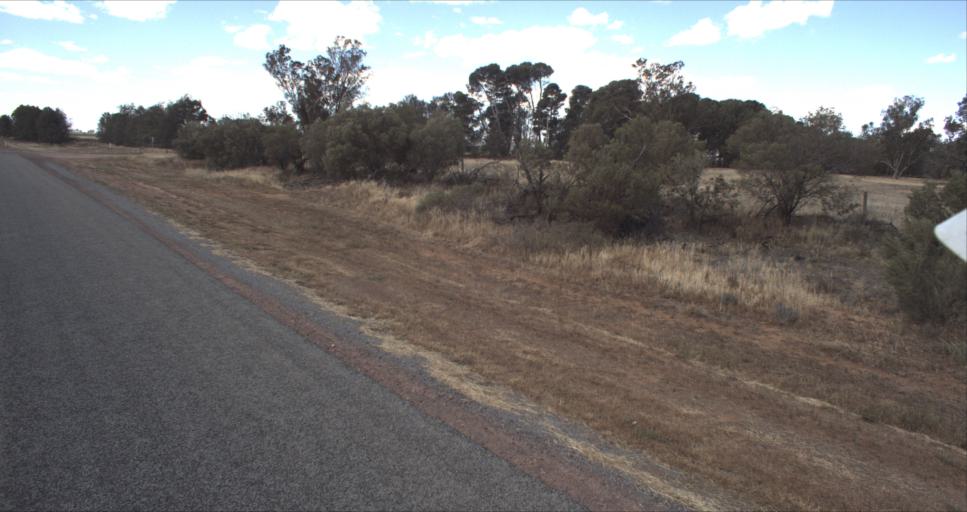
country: AU
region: New South Wales
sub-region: Leeton
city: Leeton
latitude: -34.4833
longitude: 146.2487
